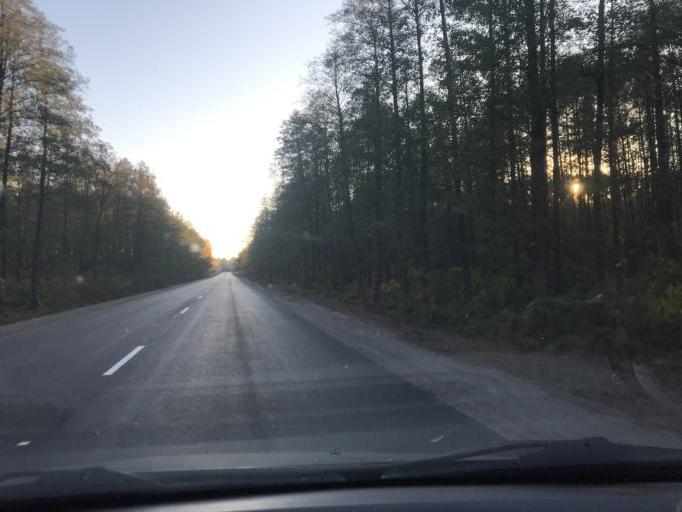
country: BY
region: Gomel
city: Brahin
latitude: 51.8654
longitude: 30.3745
